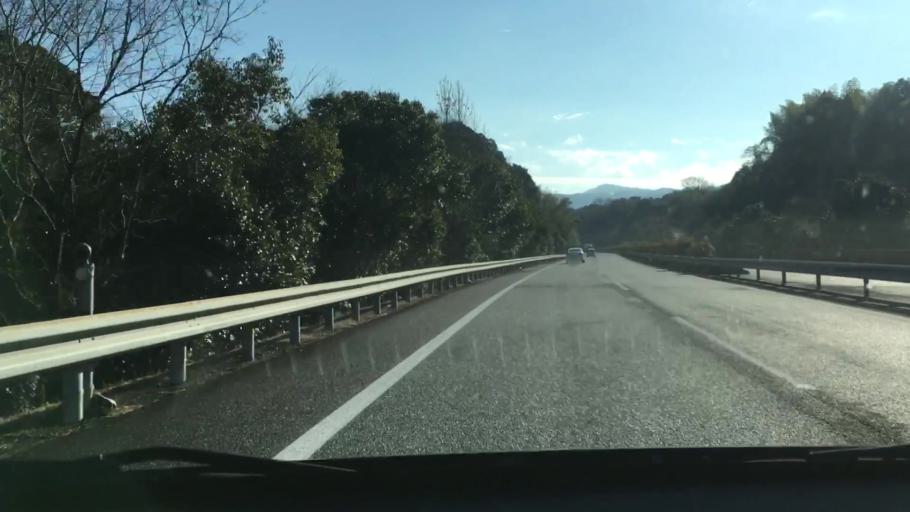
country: JP
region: Kumamoto
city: Hitoyoshi
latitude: 32.1933
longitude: 130.7777
